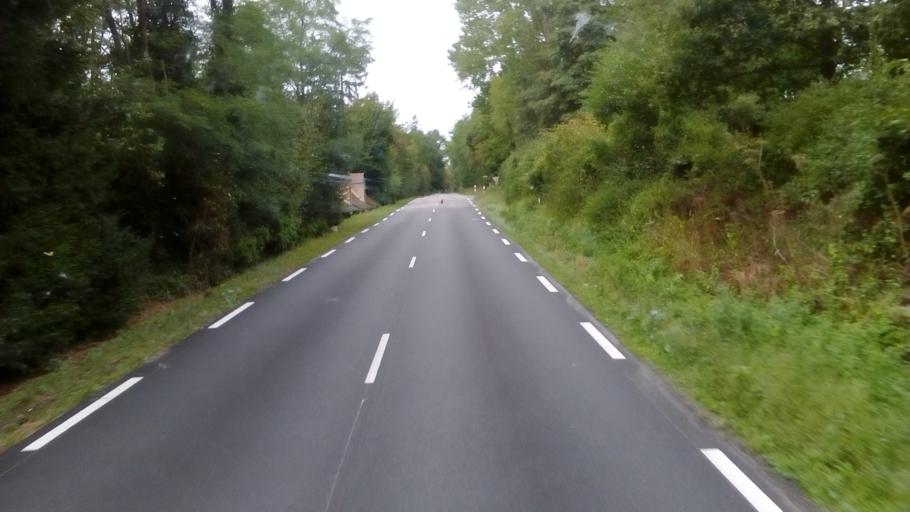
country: FR
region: Bourgogne
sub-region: Departement de Saone-et-Loire
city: Saint-Yan
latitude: 46.4334
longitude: 4.0217
